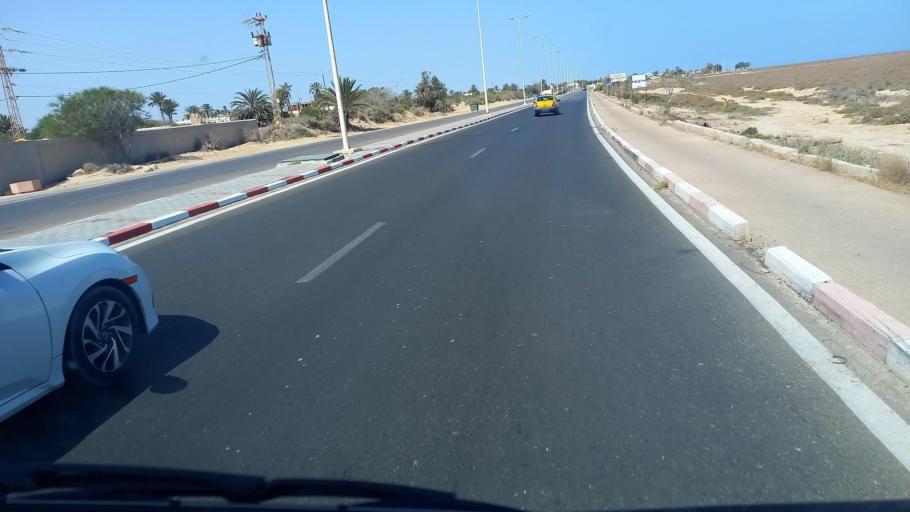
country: TN
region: Madanin
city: Midoun
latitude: 33.8689
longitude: 10.9433
